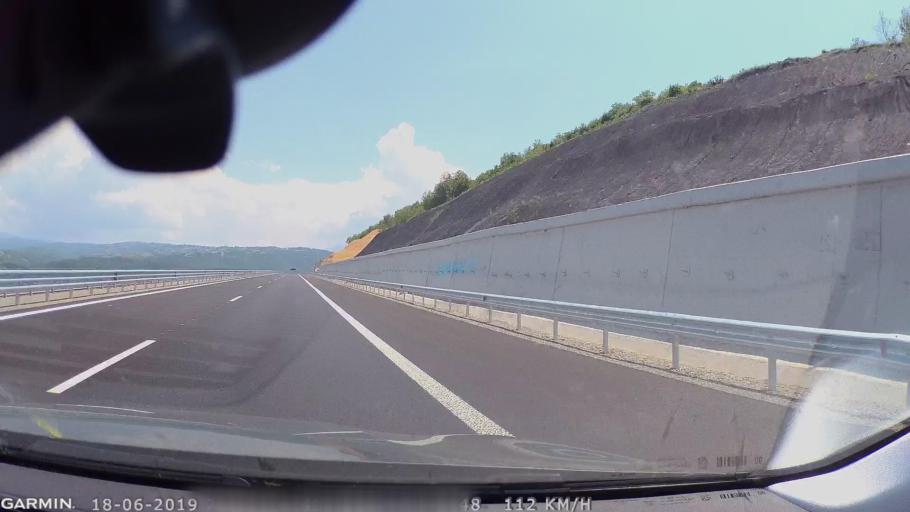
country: BG
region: Blagoevgrad
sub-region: Obshtina Blagoevgrad
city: Blagoevgrad
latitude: 41.9761
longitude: 23.0722
